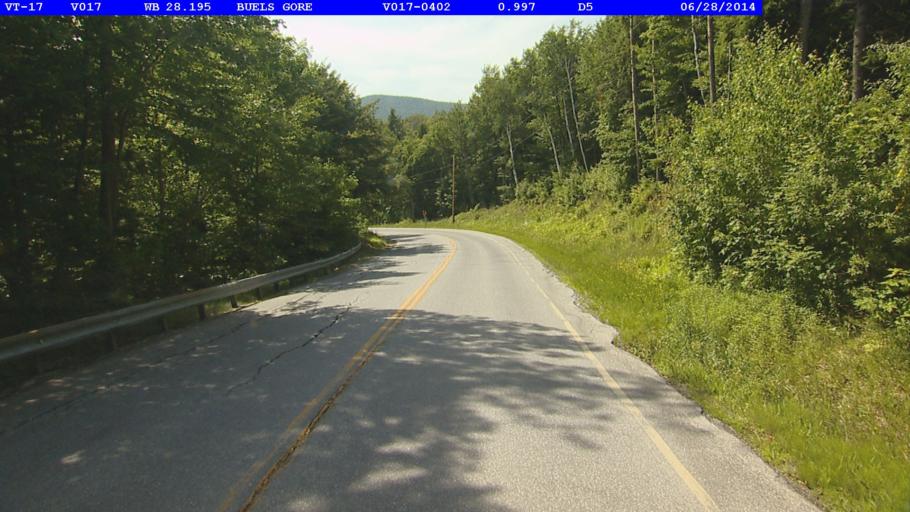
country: US
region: Vermont
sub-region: Addison County
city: Bristol
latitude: 44.2196
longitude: -72.9496
